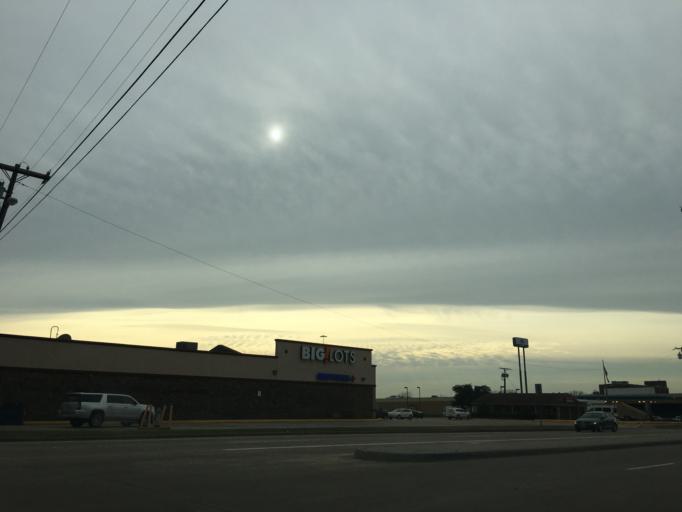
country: US
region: Texas
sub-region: Collin County
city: McKinney
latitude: 33.1986
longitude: -96.6367
